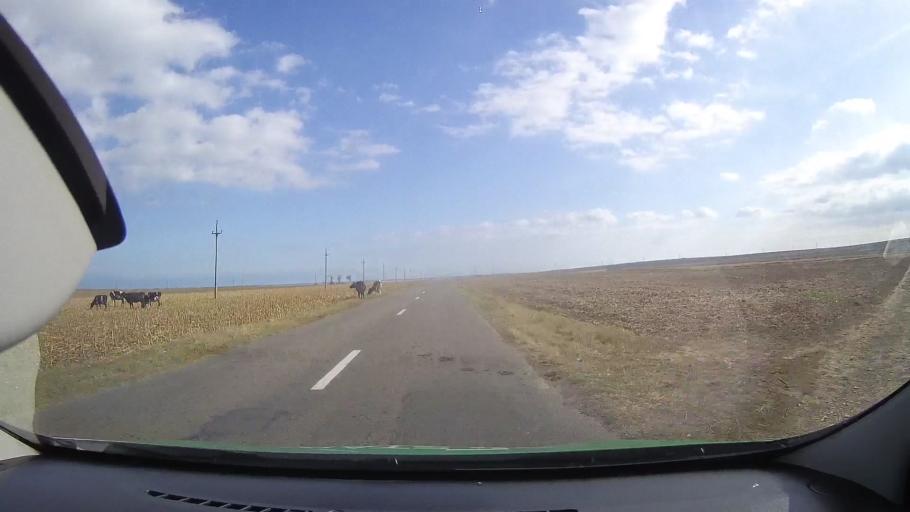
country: RO
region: Constanta
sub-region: Comuna Istria
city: Nuntasi
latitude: 44.5330
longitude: 28.6691
